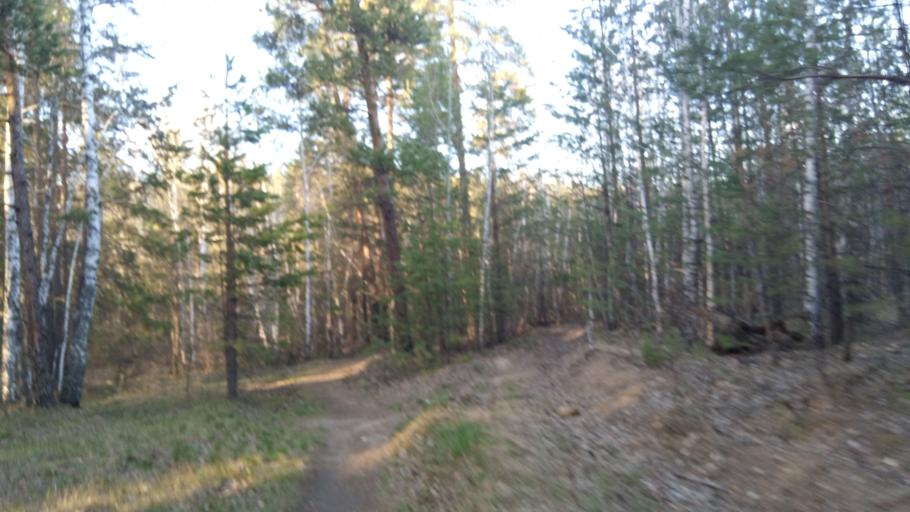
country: RU
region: Chelyabinsk
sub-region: Gorod Chelyabinsk
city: Chelyabinsk
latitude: 55.1393
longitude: 61.3379
